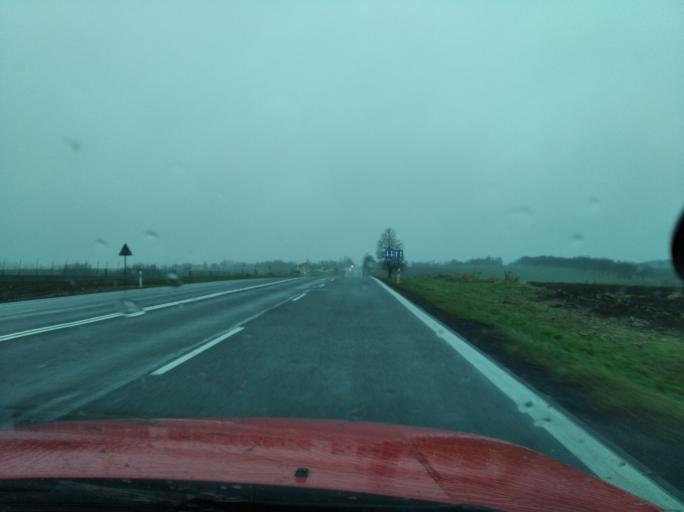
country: PL
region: Subcarpathian Voivodeship
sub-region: Powiat lancucki
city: Rogozno
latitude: 50.0672
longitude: 22.3879
